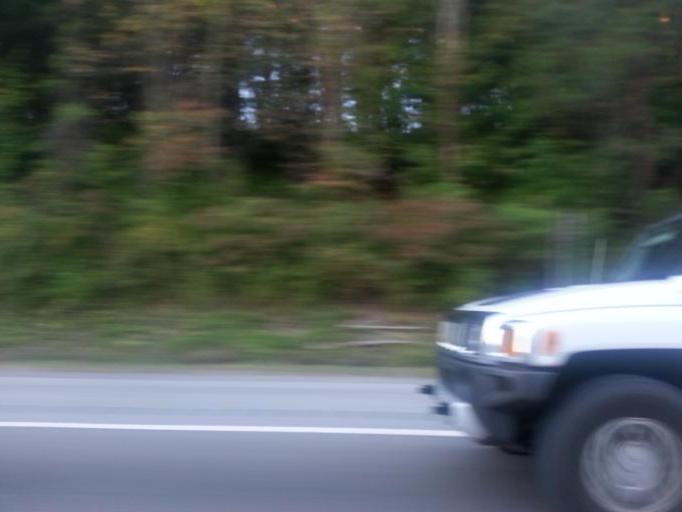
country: US
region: Tennessee
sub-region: Anderson County
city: Norris
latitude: 36.1164
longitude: -84.0293
